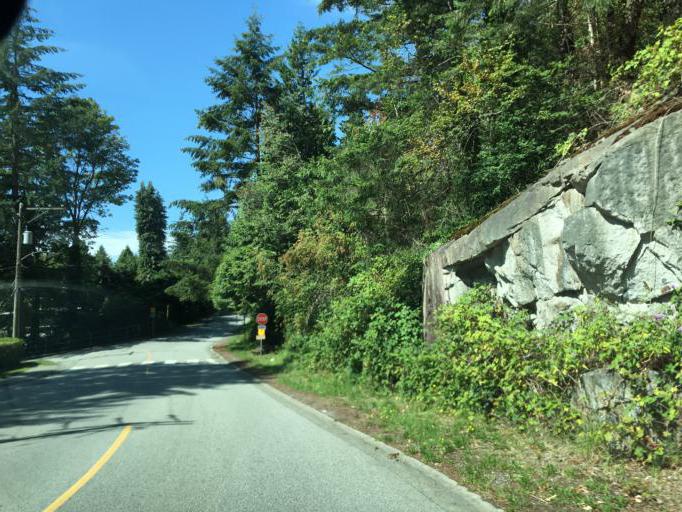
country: CA
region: British Columbia
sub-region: Greater Vancouver Regional District
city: Bowen Island
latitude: 49.3424
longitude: -123.2600
